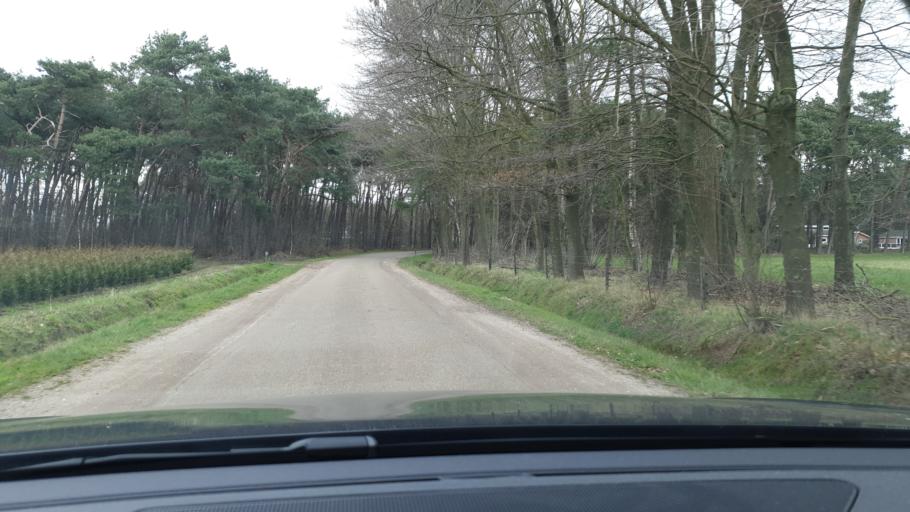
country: NL
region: North Brabant
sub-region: Gemeente Veldhoven
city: Oerle
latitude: 51.4211
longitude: 5.3487
